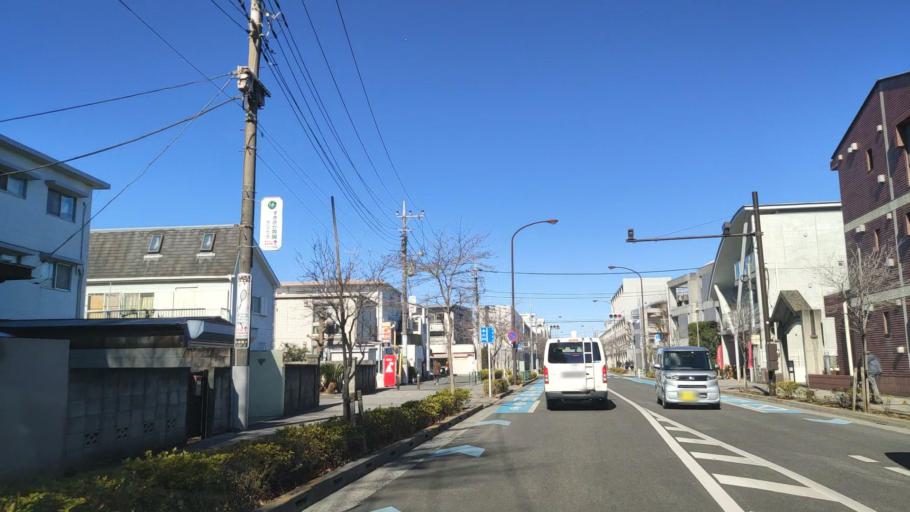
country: JP
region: Tokyo
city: Mitaka-shi
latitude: 35.6598
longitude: 139.5877
